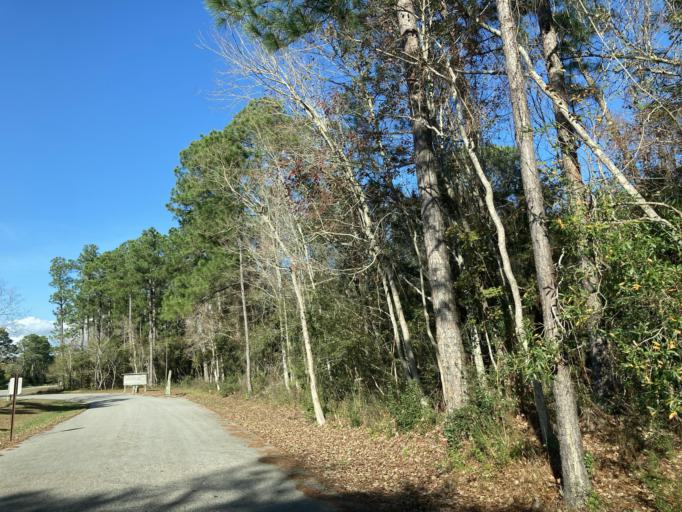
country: US
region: Mississippi
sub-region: Harrison County
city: West Gulfport
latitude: 30.4307
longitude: -89.0610
